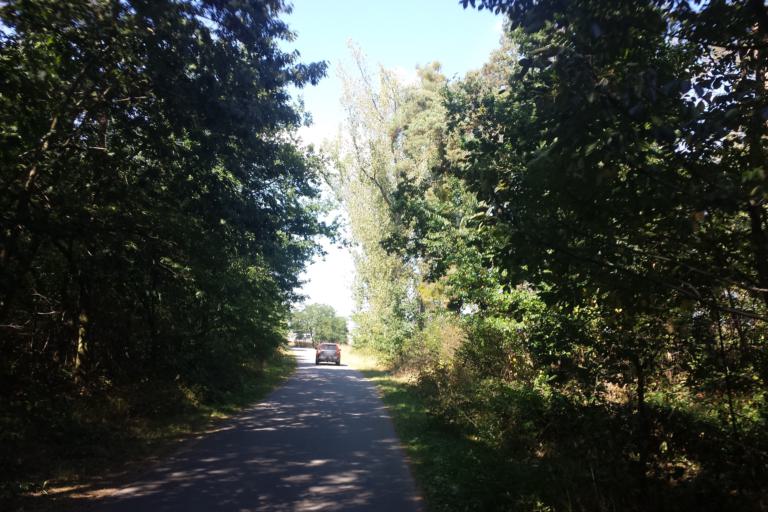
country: DE
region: Hesse
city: Lorsch
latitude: 49.6328
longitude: 8.5741
